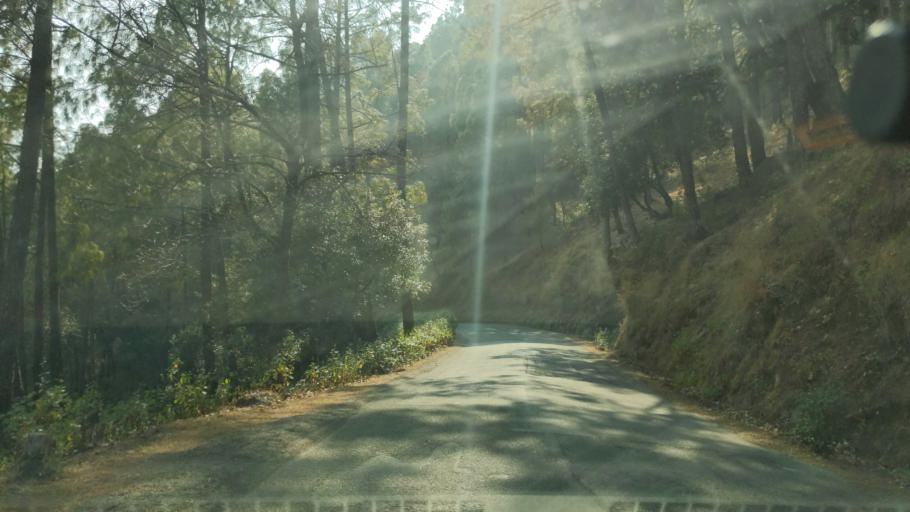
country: IN
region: Uttarakhand
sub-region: Naini Tal
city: Bhowali
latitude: 29.3930
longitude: 79.5395
